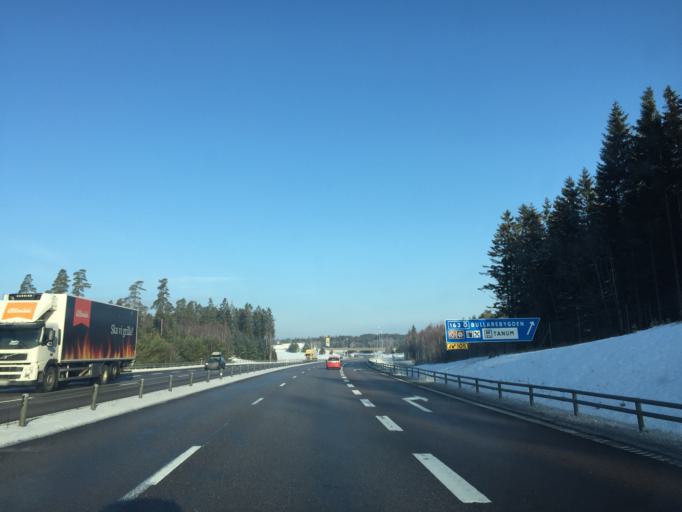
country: SE
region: Vaestra Goetaland
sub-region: Tanums Kommun
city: Tanumshede
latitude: 58.7151
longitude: 11.3545
